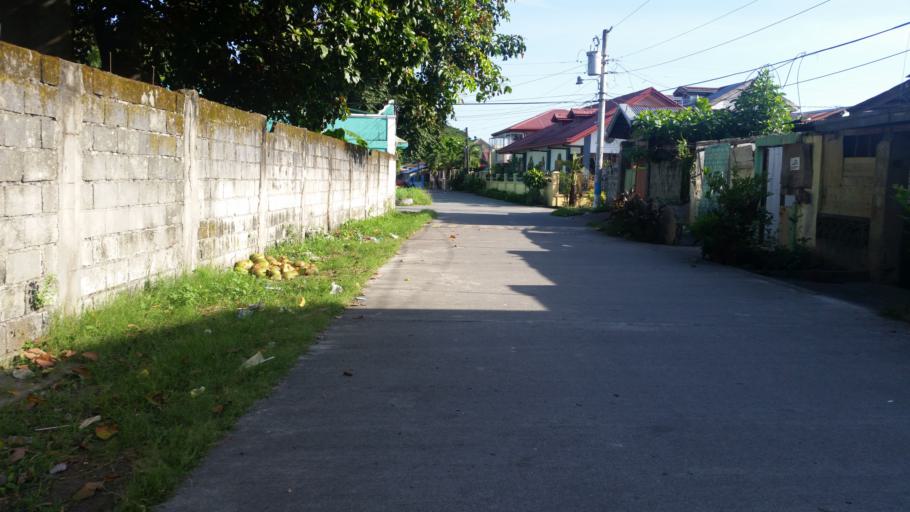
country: PH
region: Central Luzon
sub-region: Province of Pampanga
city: Mabalacat City
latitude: 15.2772
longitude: 120.5686
